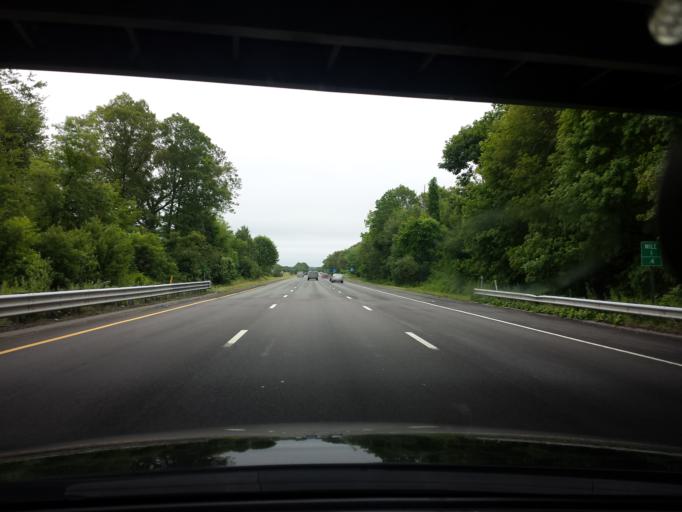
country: US
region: Massachusetts
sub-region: Bristol County
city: Seekonk
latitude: 41.7952
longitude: -71.3164
